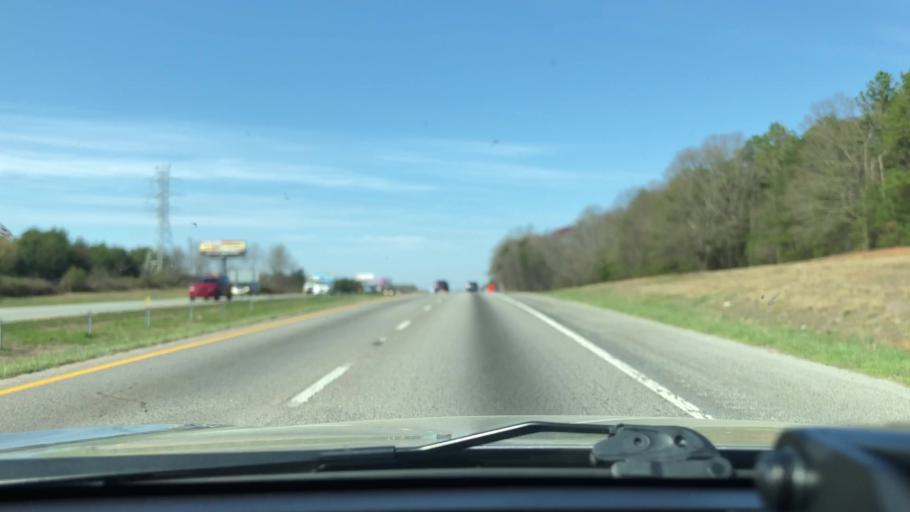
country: US
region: South Carolina
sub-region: Spartanburg County
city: Roebuck
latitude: 34.9102
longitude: -81.9903
